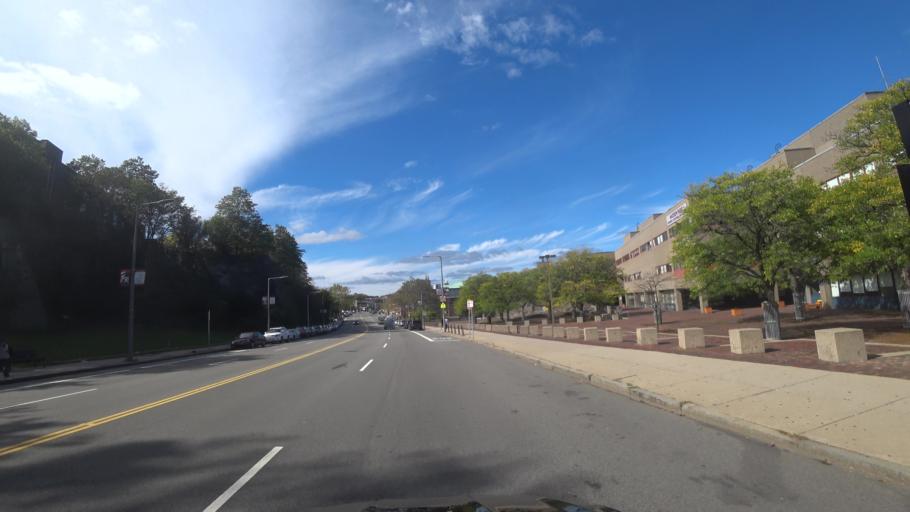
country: US
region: Massachusetts
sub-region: Norfolk County
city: Brookline
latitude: 42.3311
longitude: -71.0898
